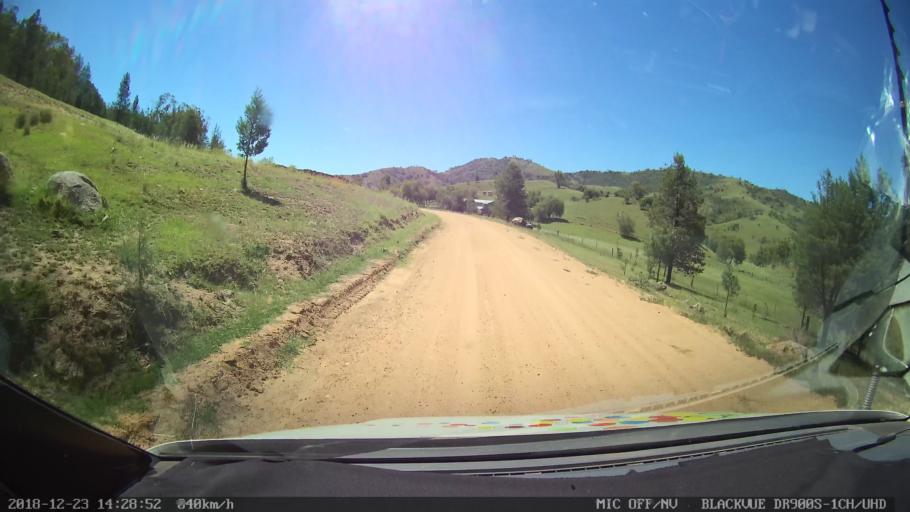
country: AU
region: New South Wales
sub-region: Tamworth Municipality
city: Manilla
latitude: -30.6120
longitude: 150.9399
